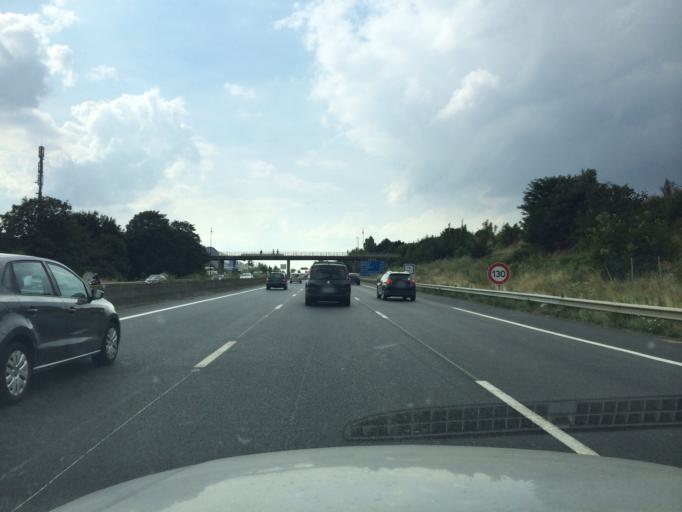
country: FR
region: Ile-de-France
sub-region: Departement des Yvelines
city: Villennes-sur-Seine
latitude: 48.9283
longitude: 1.9898
